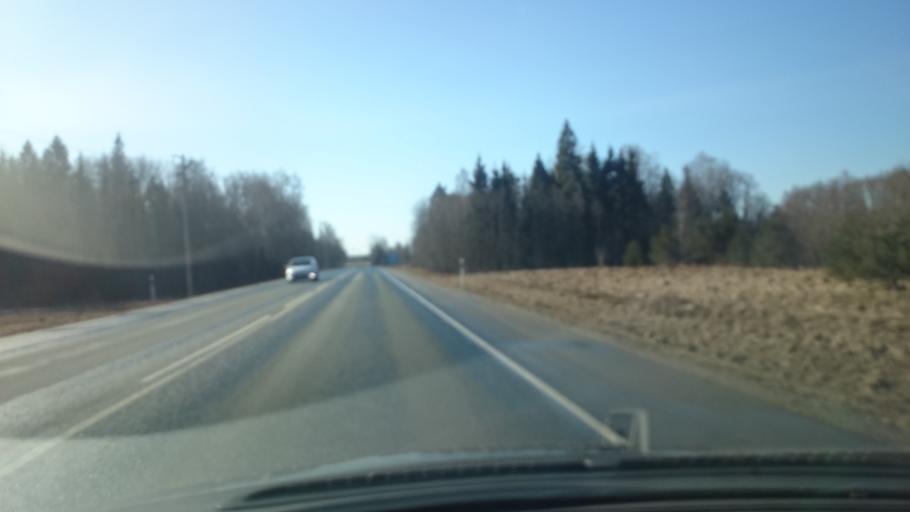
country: EE
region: Raplamaa
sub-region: Rapla vald
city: Rapla
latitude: 59.0455
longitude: 24.8386
